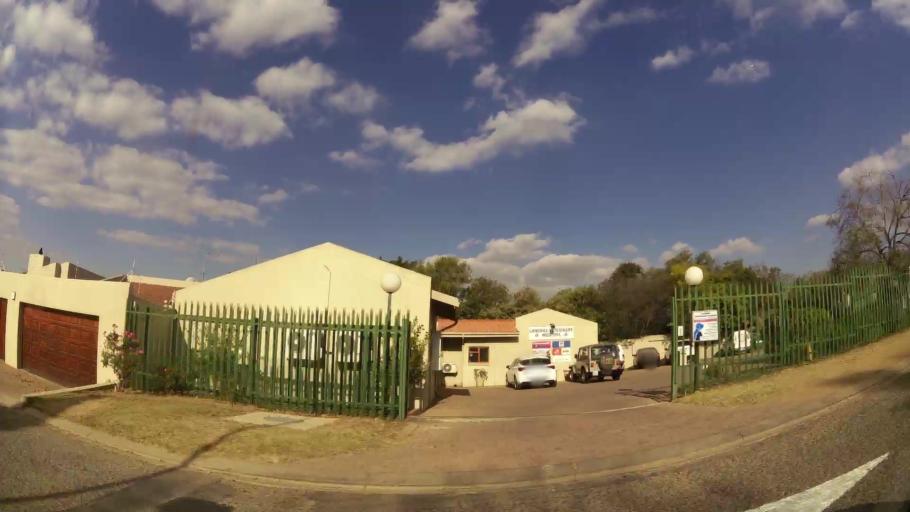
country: ZA
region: Gauteng
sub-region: City of Johannesburg Metropolitan Municipality
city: Diepsloot
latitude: -26.0103
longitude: 28.0225
